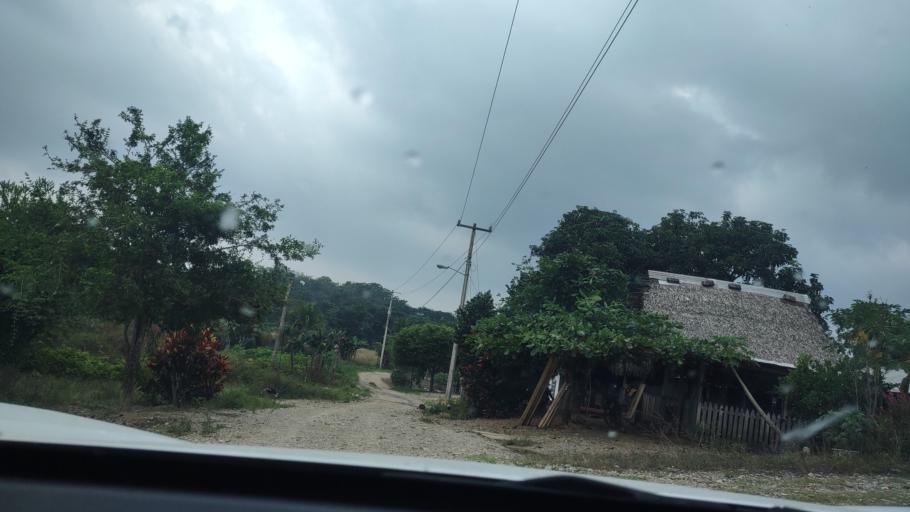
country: MX
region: Veracruz
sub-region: Uxpanapa
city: Poblado 10
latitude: 17.5482
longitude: -94.2942
